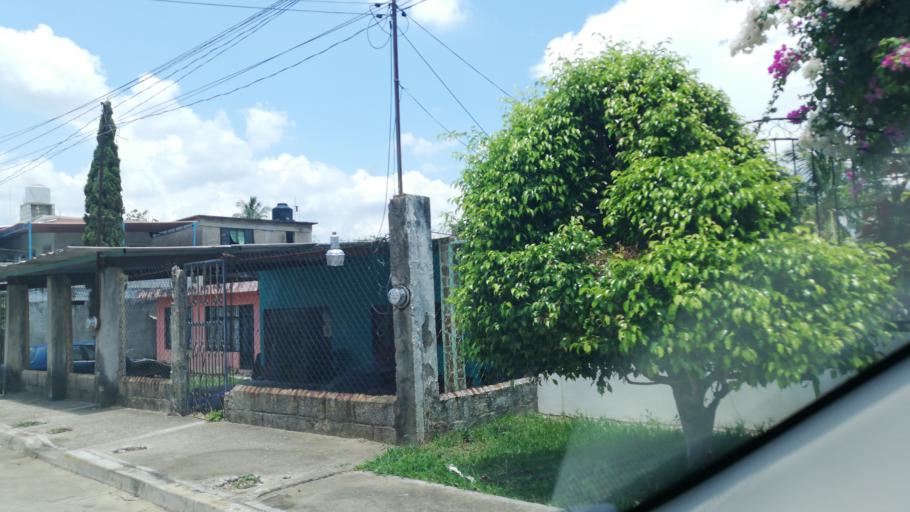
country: MX
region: Oaxaca
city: Matias Romero
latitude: 16.8847
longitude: -95.0409
